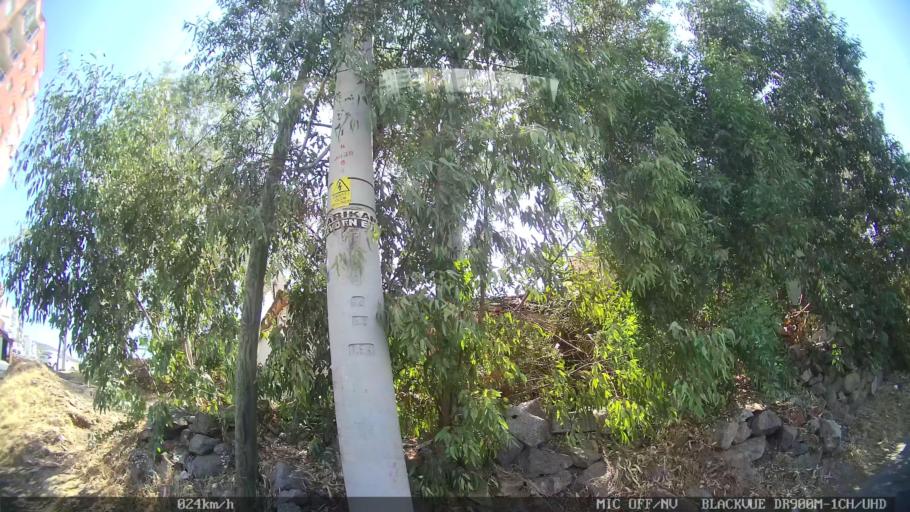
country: TR
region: Izmir
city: Karsiyaka
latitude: 38.5034
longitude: 27.0786
